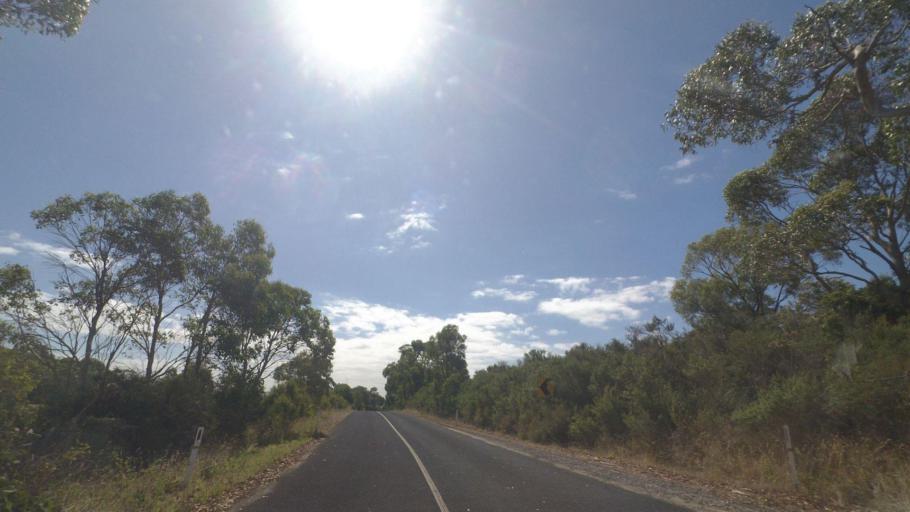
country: AU
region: Victoria
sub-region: Cardinia
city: Bunyip
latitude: -38.2957
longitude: 145.6697
